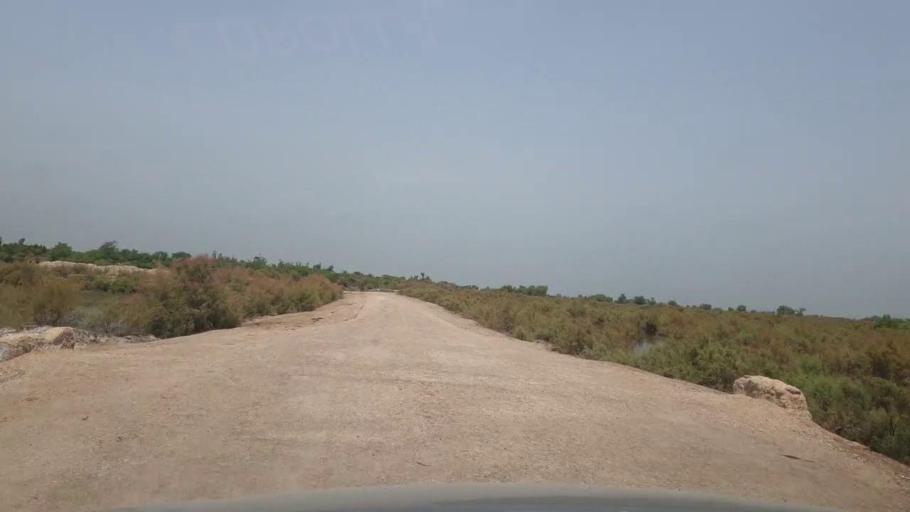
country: PK
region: Sindh
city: Garhi Yasin
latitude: 27.9178
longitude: 68.3768
